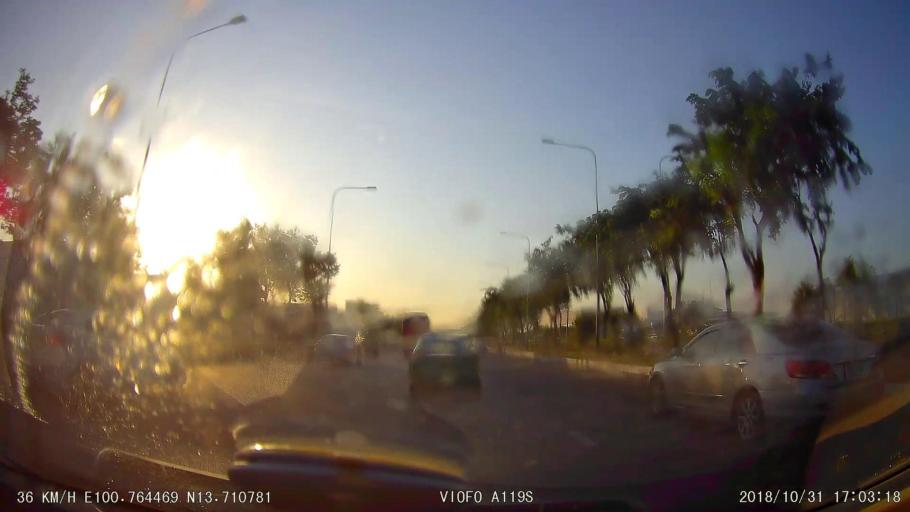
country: TH
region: Bangkok
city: Lat Krabang
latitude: 13.7108
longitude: 100.7644
